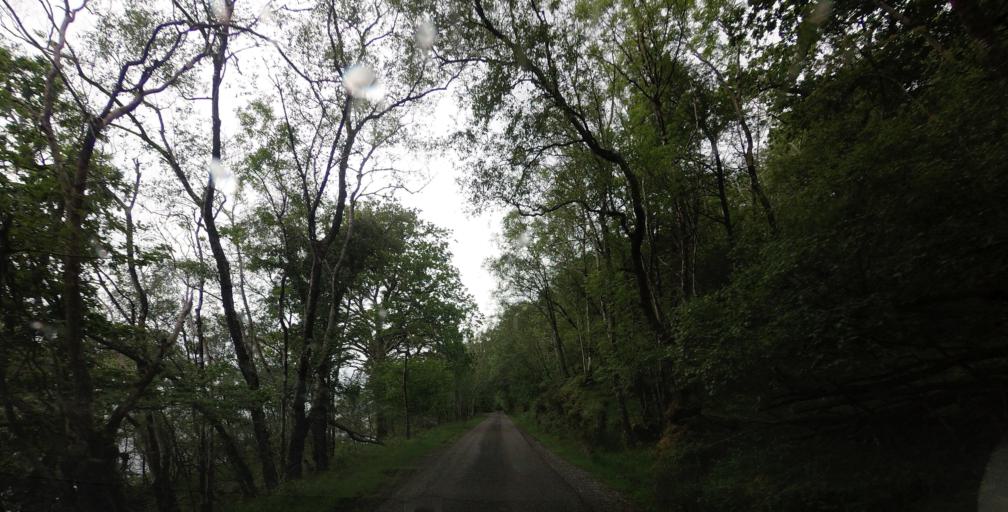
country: GB
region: Scotland
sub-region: Highland
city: Fort William
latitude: 56.7858
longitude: -5.1848
